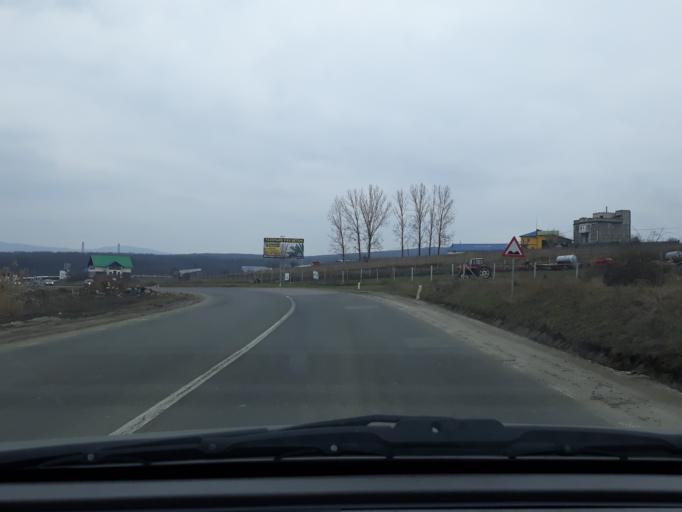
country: RO
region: Salaj
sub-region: Comuna Hereclean
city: Hereclean
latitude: 47.2305
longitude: 22.9981
